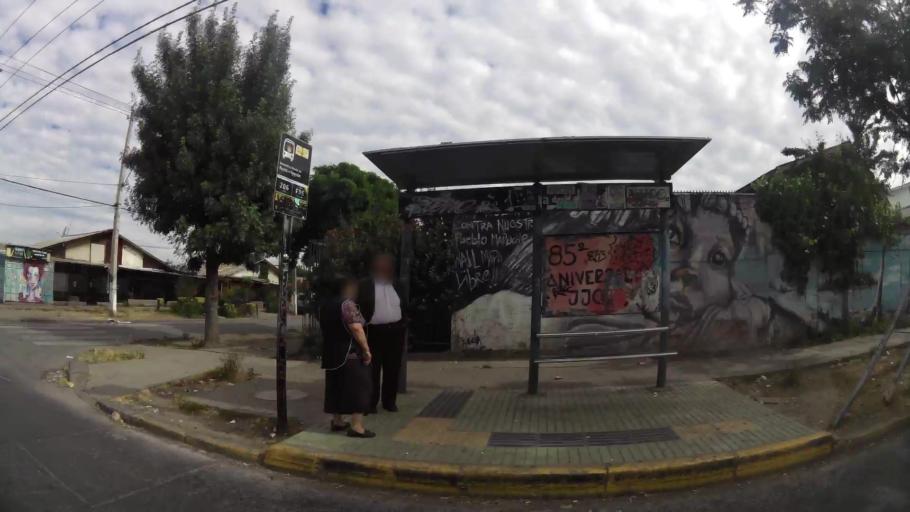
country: CL
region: Santiago Metropolitan
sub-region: Provincia de Santiago
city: La Pintana
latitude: -33.5795
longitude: -70.6425
